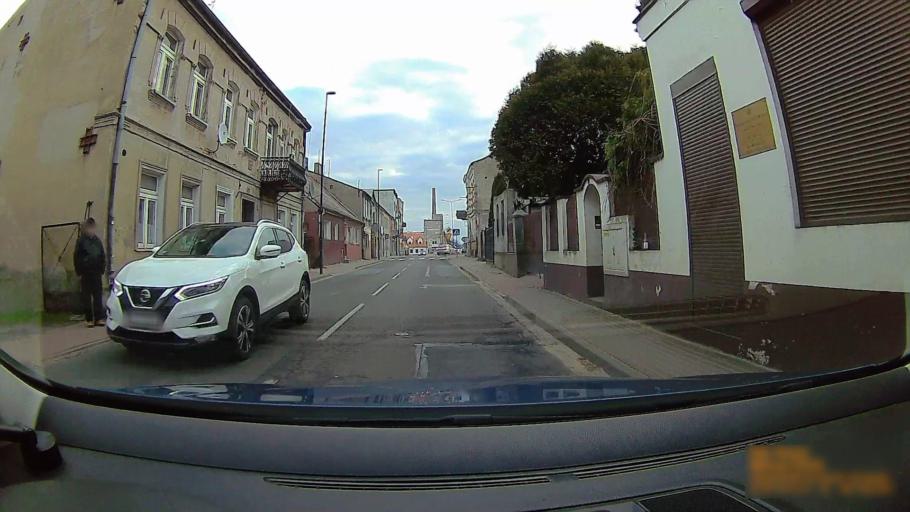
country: PL
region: Greater Poland Voivodeship
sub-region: Konin
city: Konin
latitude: 52.2048
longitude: 18.2509
